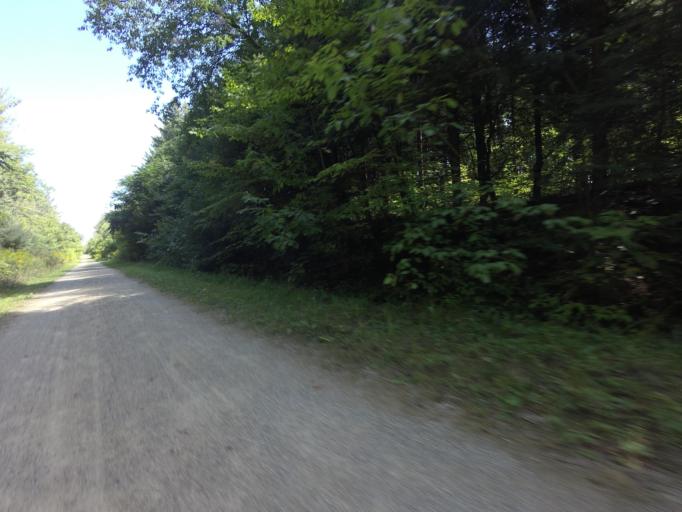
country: CA
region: Ontario
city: Orangeville
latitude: 43.7765
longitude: -80.1770
